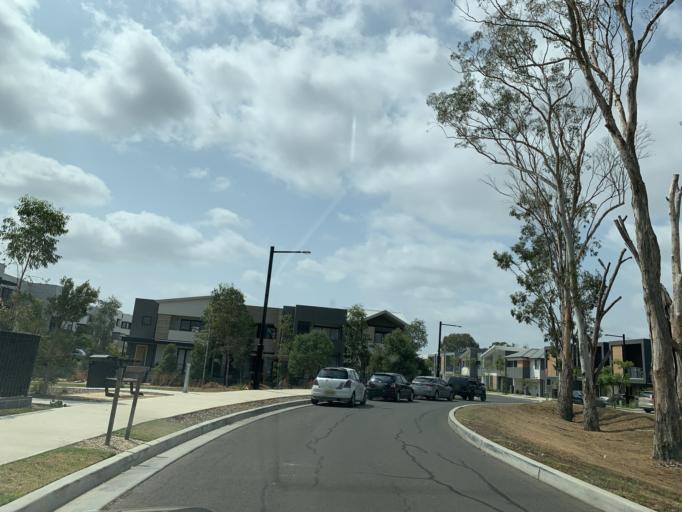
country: AU
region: New South Wales
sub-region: Blacktown
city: Blacktown
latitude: -33.7602
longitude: 150.8993
